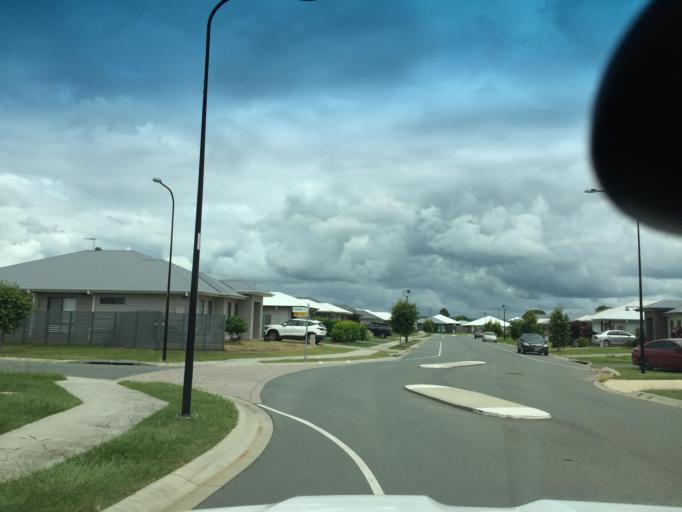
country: AU
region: Queensland
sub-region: Moreton Bay
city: Caboolture South
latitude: -27.0967
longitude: 152.9577
